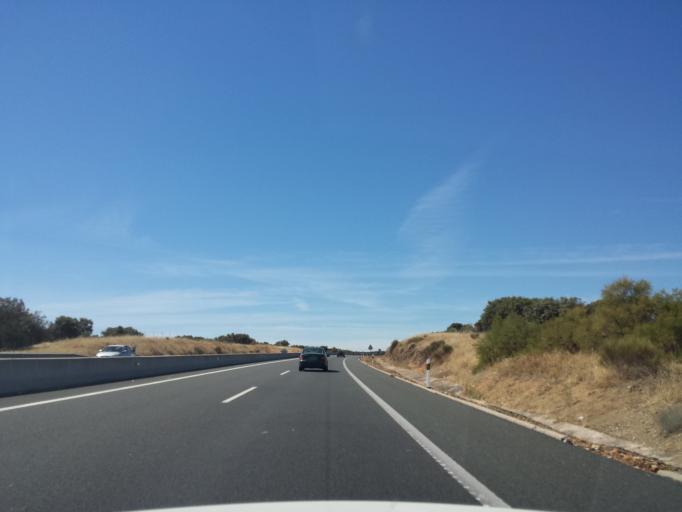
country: ES
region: Extremadura
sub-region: Provincia de Caceres
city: Jaraicejo
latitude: 39.6390
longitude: -5.8104
